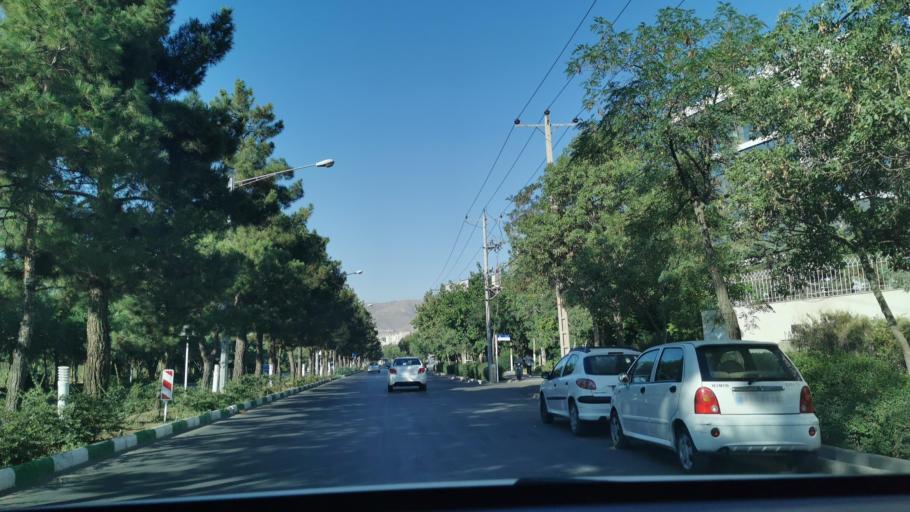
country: IR
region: Razavi Khorasan
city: Mashhad
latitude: 36.3151
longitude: 59.5253
